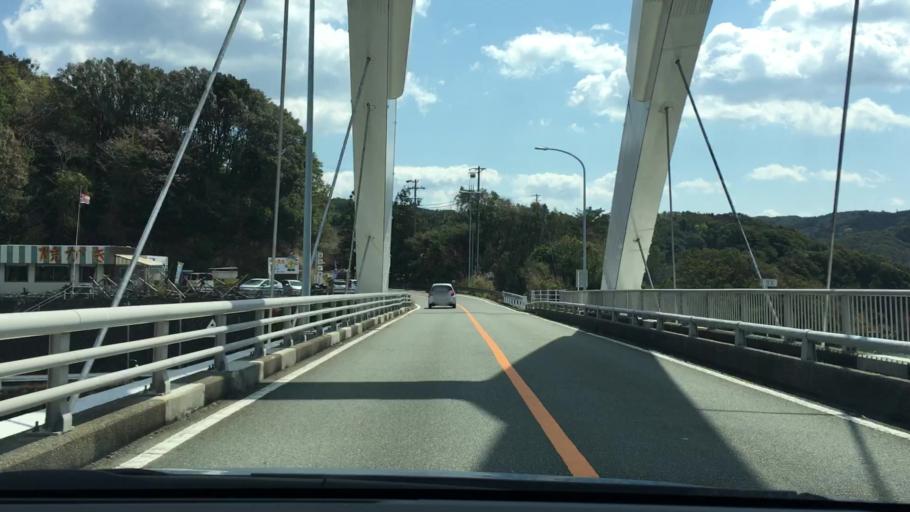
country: JP
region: Mie
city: Toba
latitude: 34.4402
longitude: 136.8824
